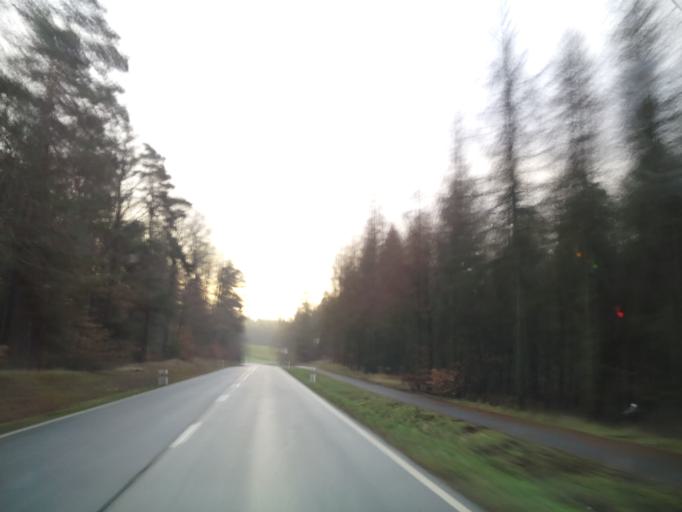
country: DE
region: Bavaria
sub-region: Upper Franconia
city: Lichtenfels
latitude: 50.1768
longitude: 11.0210
